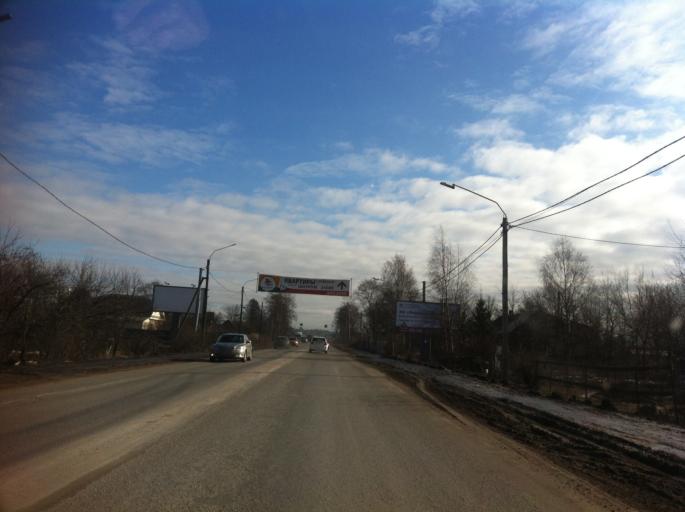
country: RU
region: Leningrad
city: Yanino Vtoroye
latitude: 59.9464
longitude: 30.5678
